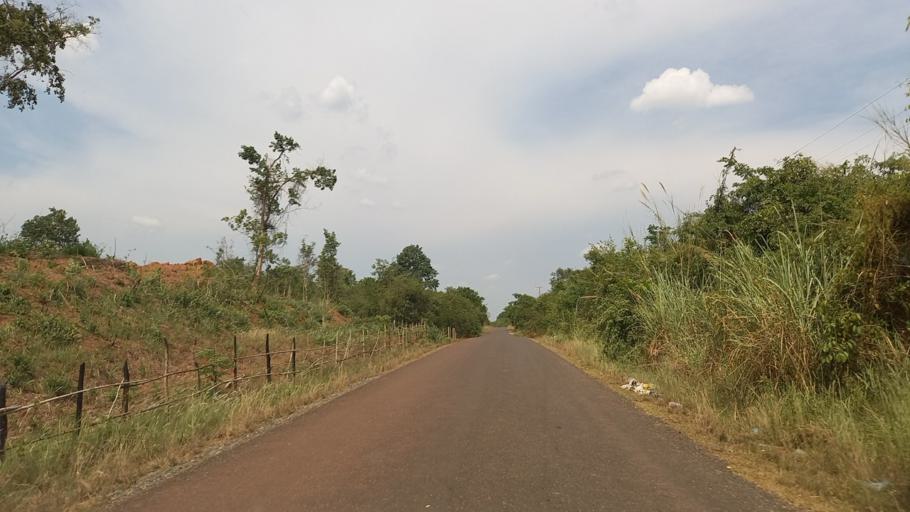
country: LA
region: Bolikhamxai
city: Muang Pakxan
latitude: 18.4289
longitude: 103.7287
